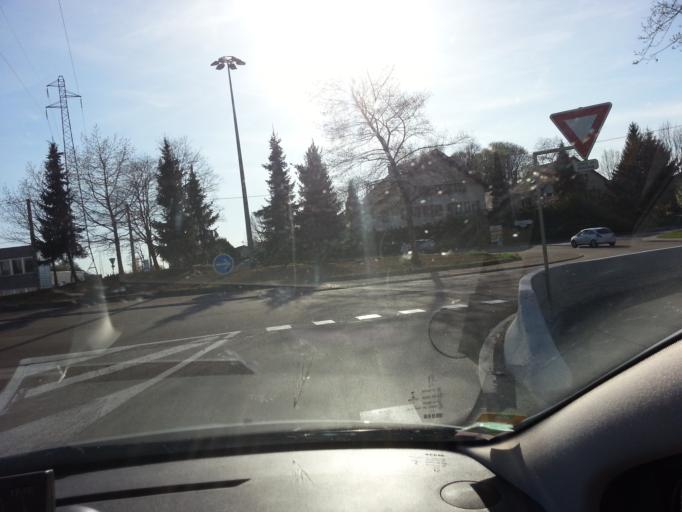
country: FR
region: Franche-Comte
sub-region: Departement du Doubs
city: Miserey-Salines
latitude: 47.2718
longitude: 5.9976
